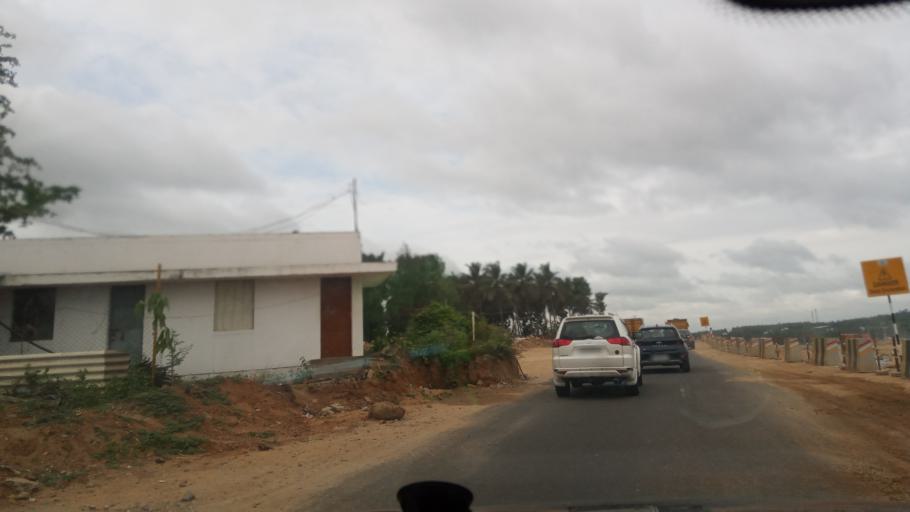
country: IN
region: Karnataka
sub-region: Mandya
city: Pandavapura
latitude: 12.4730
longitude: 76.7615
